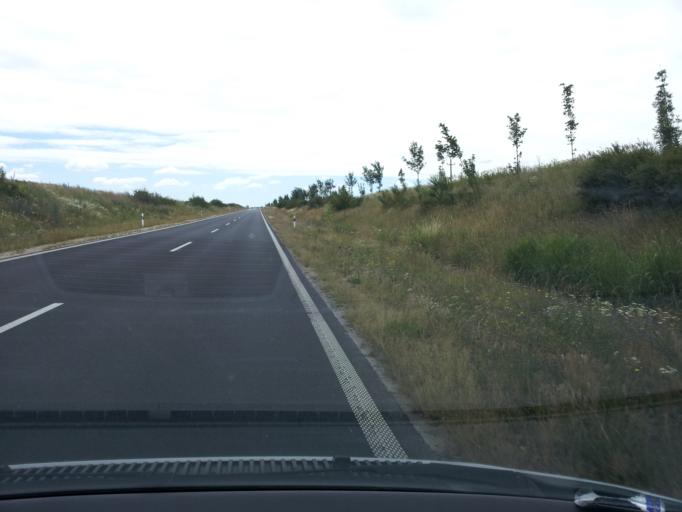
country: HU
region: Veszprem
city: Balatonkenese
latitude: 47.0722
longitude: 18.0734
